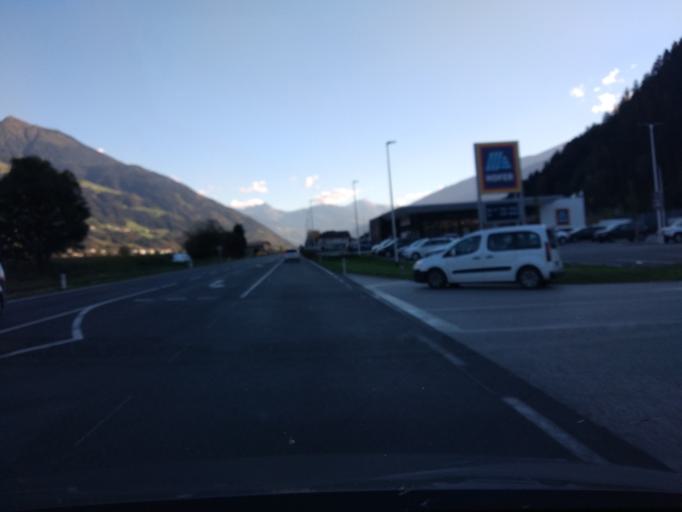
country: AT
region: Tyrol
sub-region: Politischer Bezirk Schwaz
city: Schlitters
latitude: 47.3667
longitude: 11.8499
